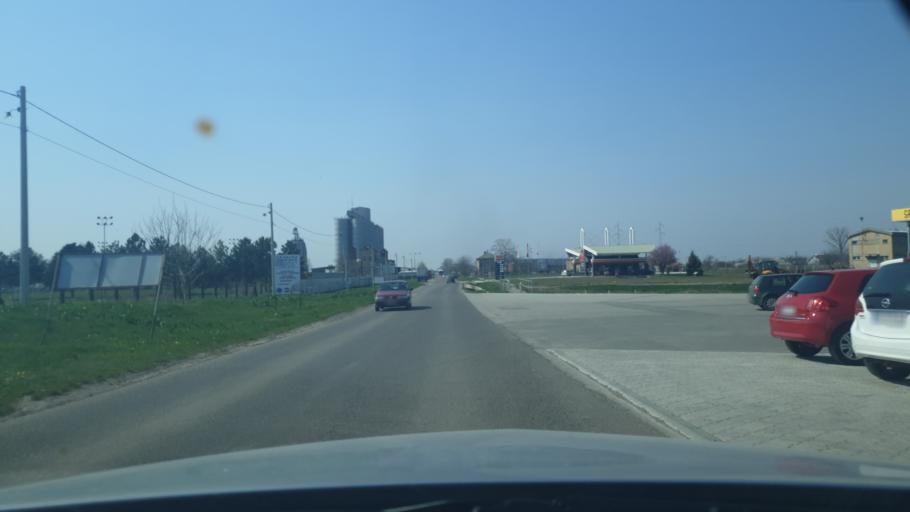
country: RS
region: Autonomna Pokrajina Vojvodina
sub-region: Sremski Okrug
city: Ruma
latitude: 45.0082
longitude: 19.7913
